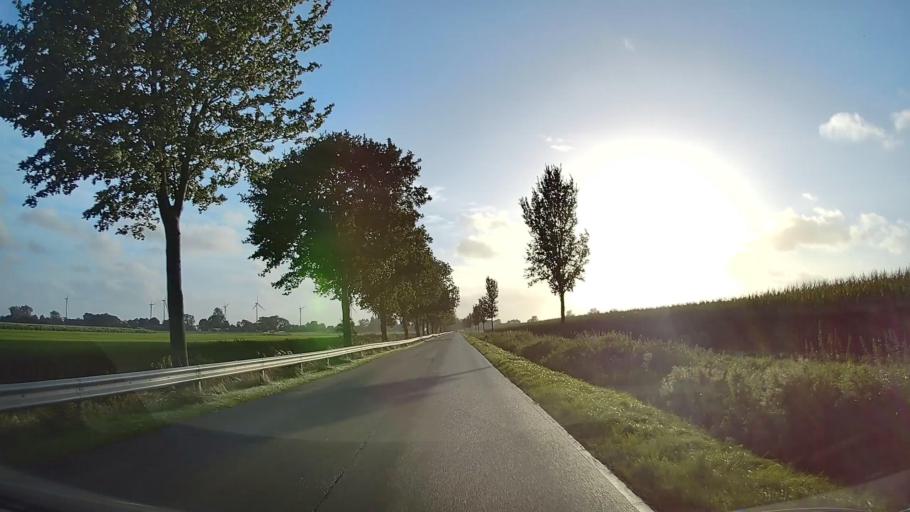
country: DE
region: Schleswig-Holstein
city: Sommerland
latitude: 53.8097
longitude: 9.5457
